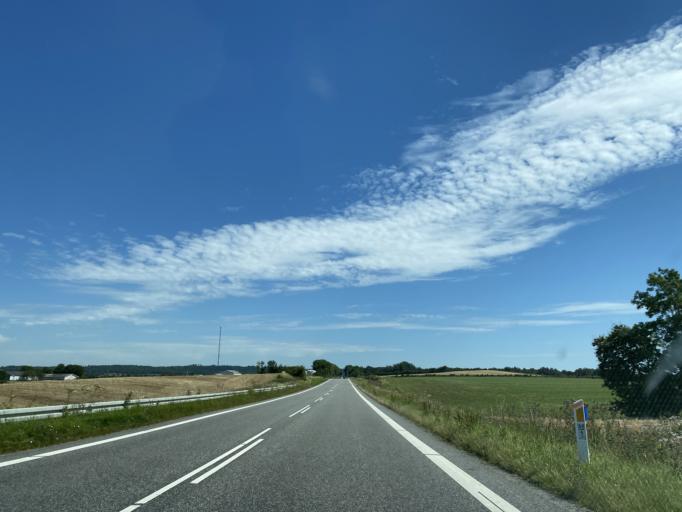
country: DK
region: South Denmark
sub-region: Faaborg-Midtfyn Kommune
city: Faaborg
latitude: 55.1090
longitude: 10.2039
